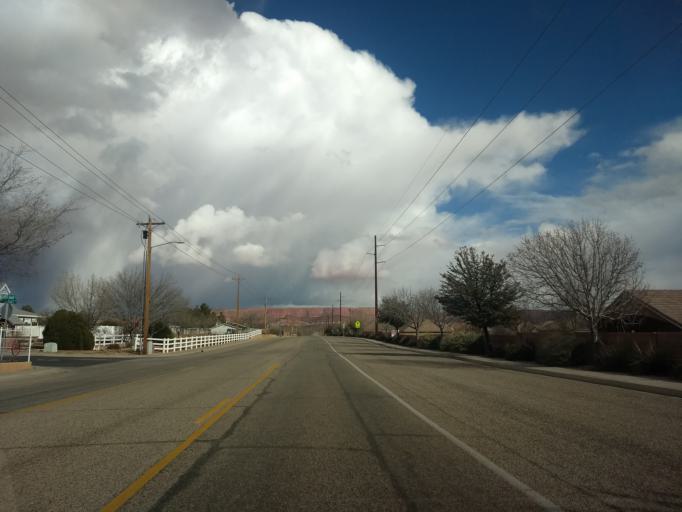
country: US
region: Utah
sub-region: Washington County
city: Saint George
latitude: 37.0668
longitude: -113.5383
